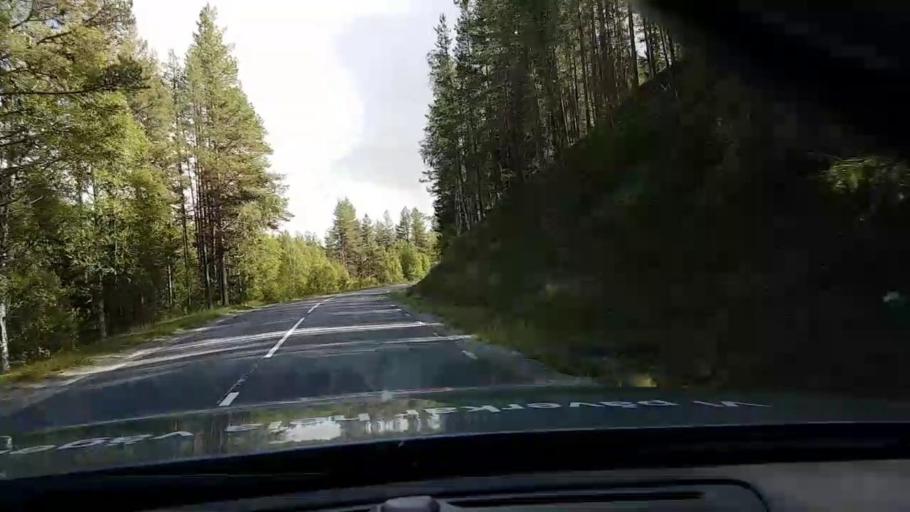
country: SE
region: Vaesterbotten
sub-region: Asele Kommun
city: Asele
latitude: 63.8586
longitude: 17.3826
